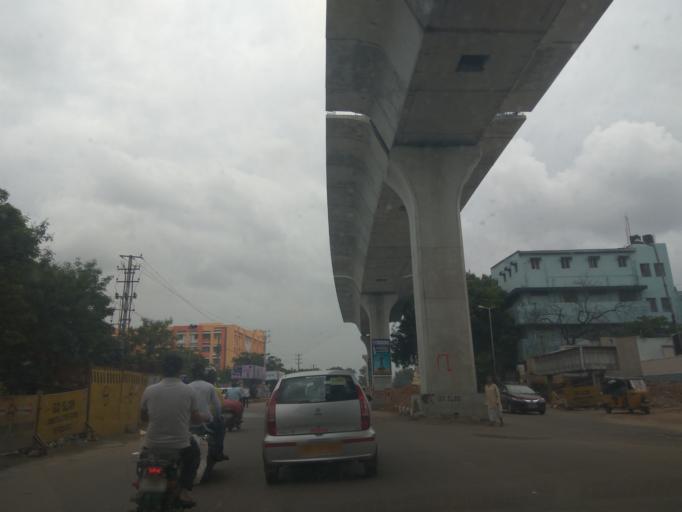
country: IN
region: Telangana
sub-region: Hyderabad
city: Malkajgiri
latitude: 17.4249
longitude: 78.5019
